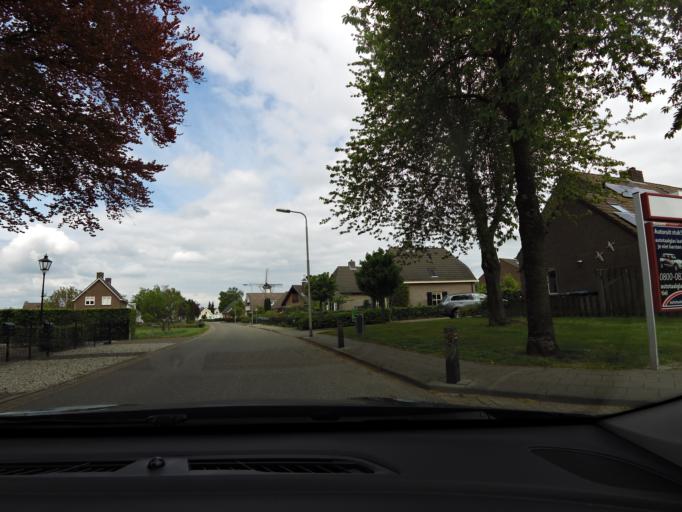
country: NL
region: Gelderland
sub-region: Gemeente Buren
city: Lienden
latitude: 51.9580
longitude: 5.4820
